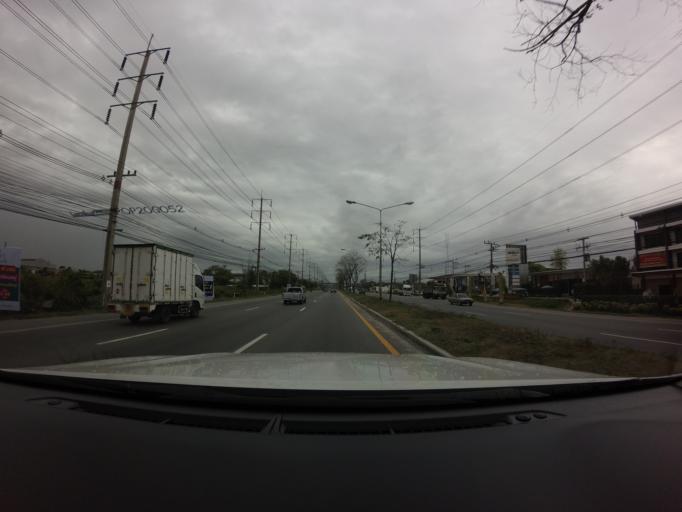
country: TH
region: Chachoengsao
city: Bang Pakong
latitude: 13.5828
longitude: 101.0086
